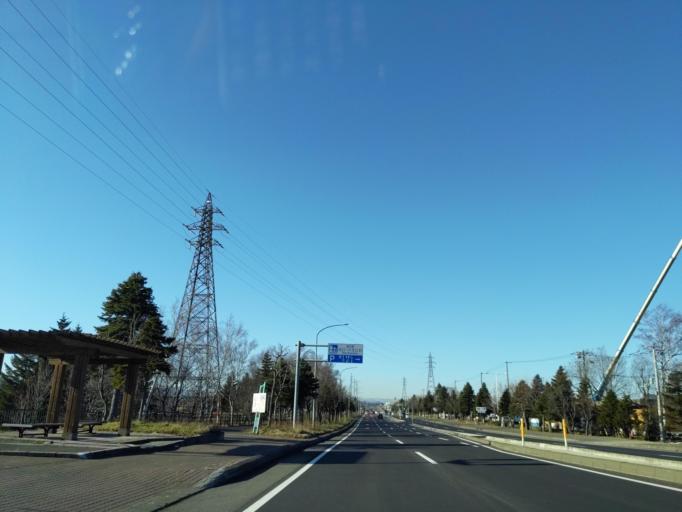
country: JP
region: Hokkaido
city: Kitahiroshima
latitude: 42.8960
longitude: 141.5867
